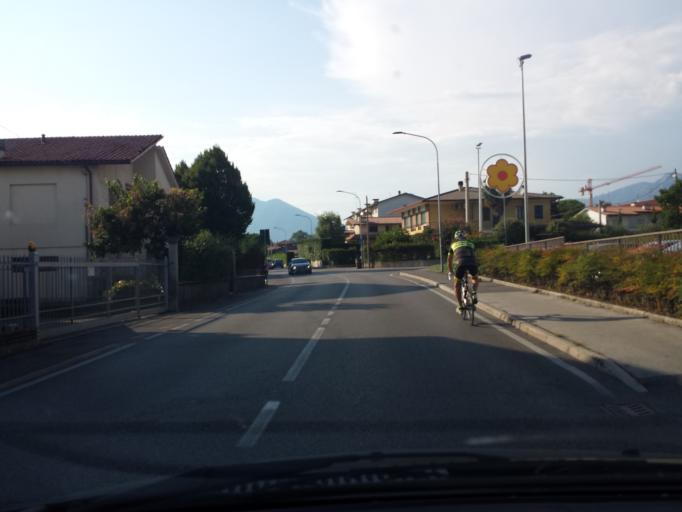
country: IT
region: Veneto
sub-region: Provincia di Vicenza
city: Thiene
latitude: 45.7005
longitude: 11.4893
